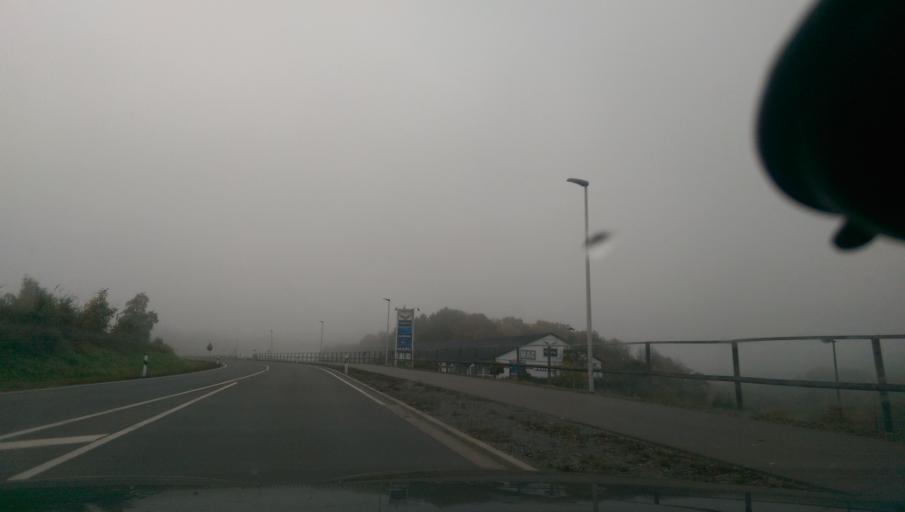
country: DE
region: Bavaria
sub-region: Regierungsbezirk Unterfranken
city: Bad Kissingen
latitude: 50.1809
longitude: 10.0788
